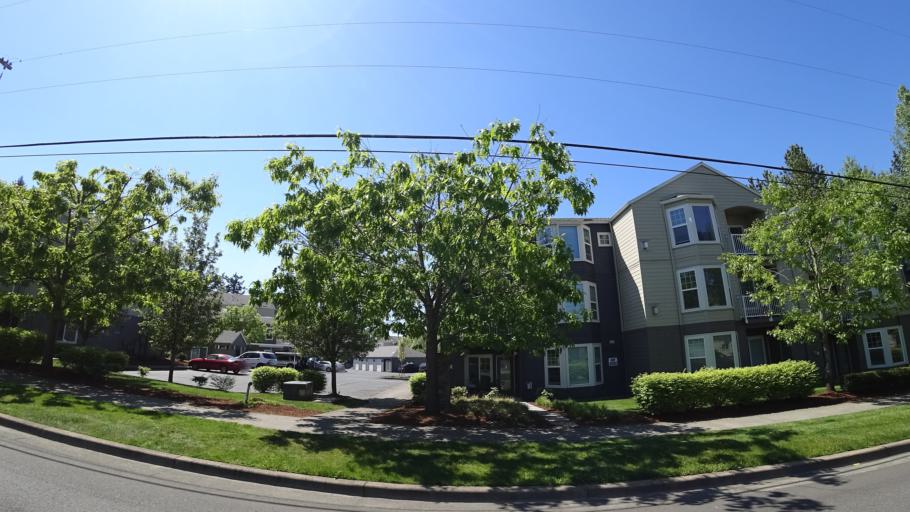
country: US
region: Oregon
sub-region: Washington County
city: Raleigh Hills
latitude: 45.4845
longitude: -122.7609
